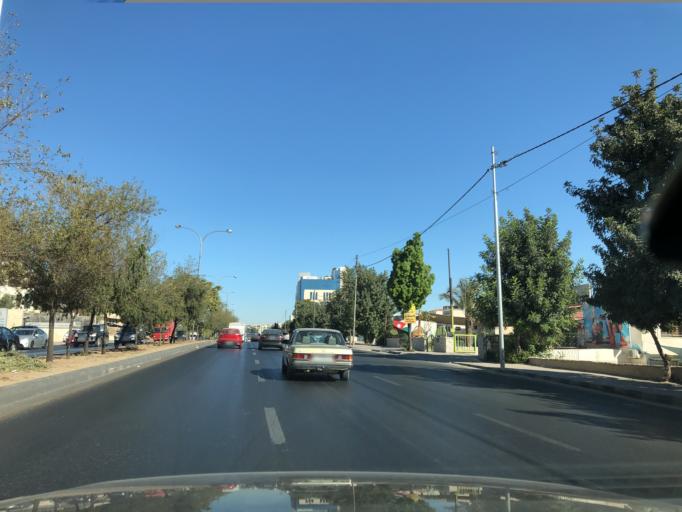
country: JO
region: Amman
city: Wadi as Sir
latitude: 31.9681
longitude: 35.8419
